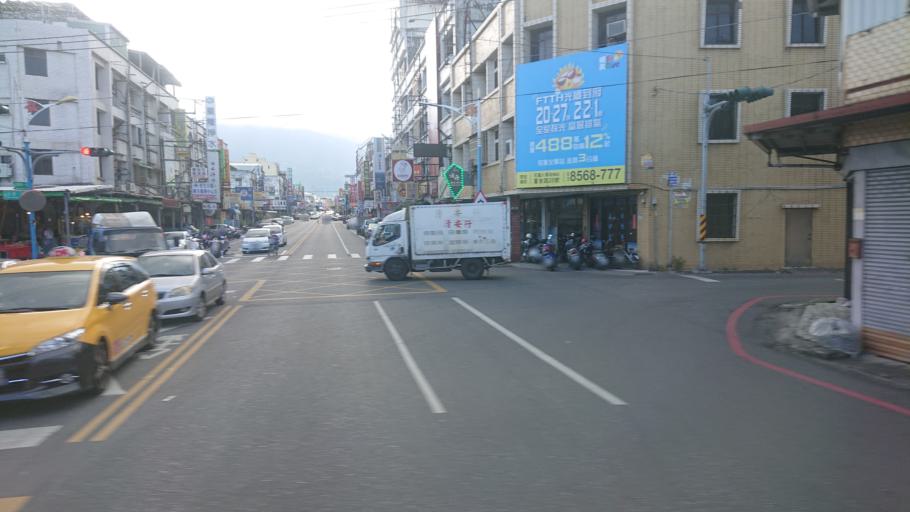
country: TW
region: Taiwan
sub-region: Hualien
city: Hualian
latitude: 23.9848
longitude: 121.5969
